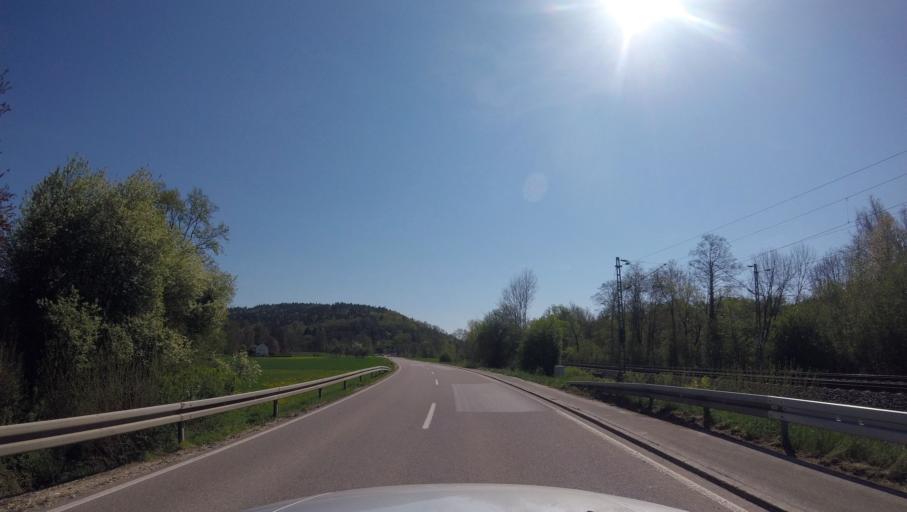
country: DE
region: Baden-Wuerttemberg
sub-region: Regierungsbezirk Stuttgart
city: Lorch
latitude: 48.7973
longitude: 9.7121
